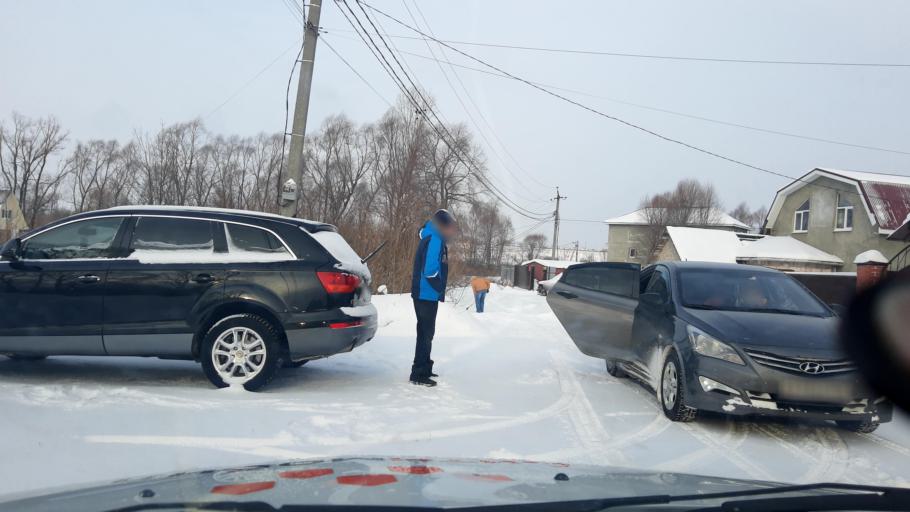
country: RU
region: Bashkortostan
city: Mikhaylovka
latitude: 54.7939
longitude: 55.8945
